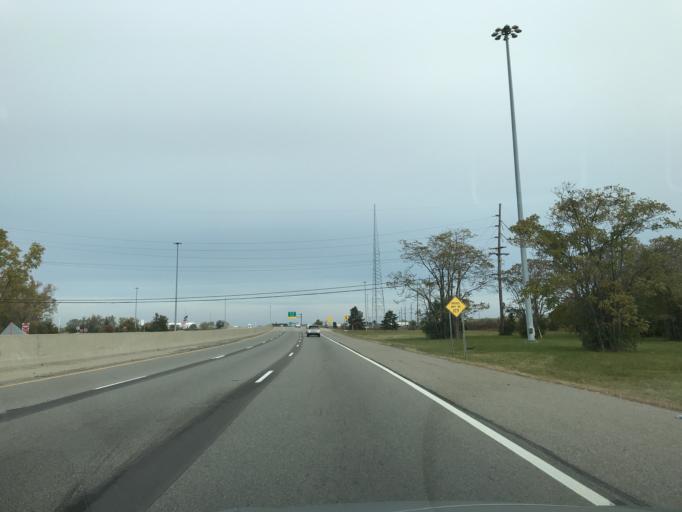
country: US
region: Michigan
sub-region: Oakland County
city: Bingham Farms
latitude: 42.4855
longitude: -83.2848
